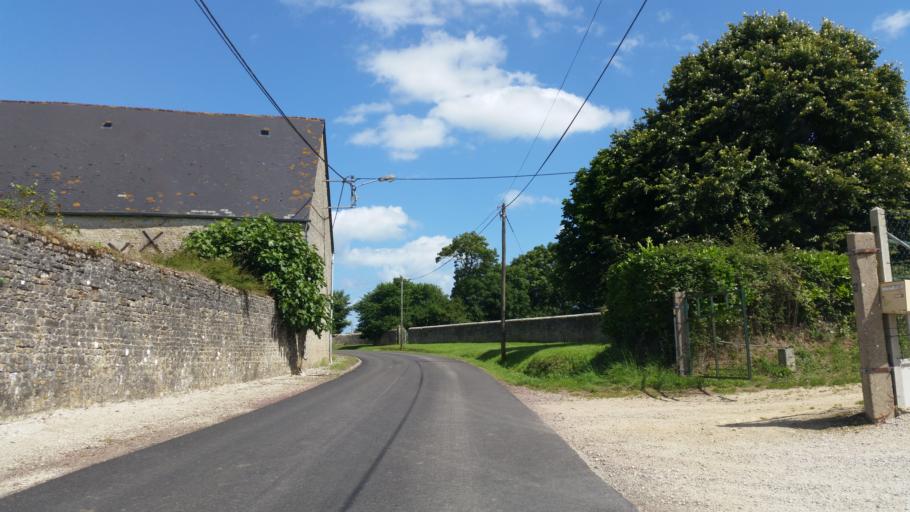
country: FR
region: Lower Normandy
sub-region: Departement de la Manche
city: Sainte-Mere-Eglise
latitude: 49.4582
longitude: -1.3167
